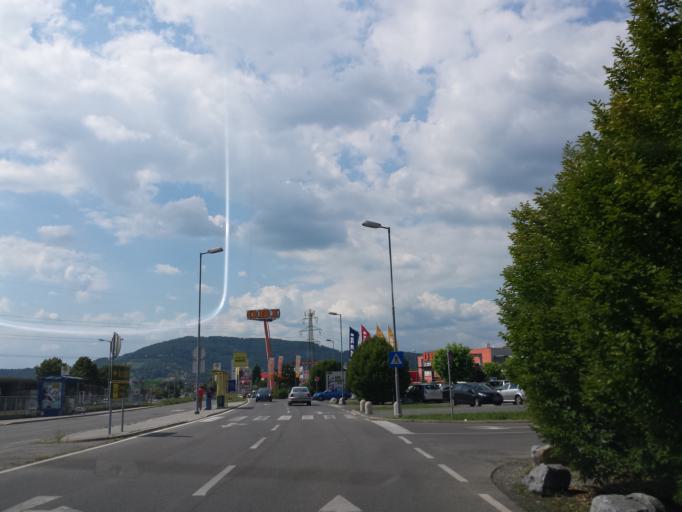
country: AT
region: Styria
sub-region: Graz Stadt
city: Wetzelsdorf
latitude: 47.0322
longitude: 15.4224
